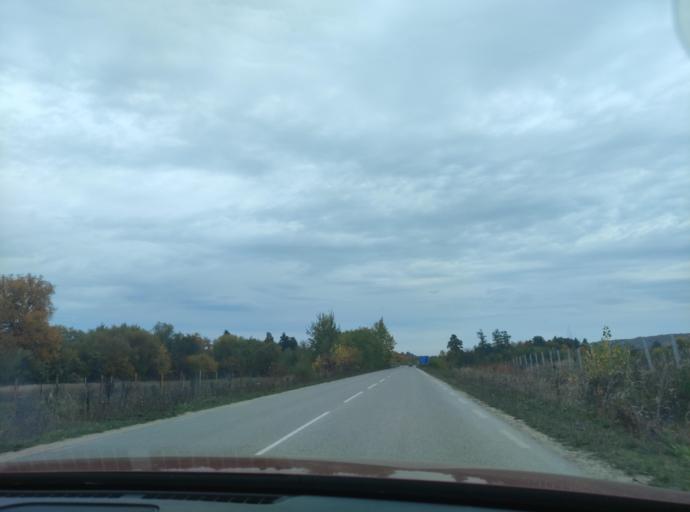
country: BG
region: Montana
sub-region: Obshtina Berkovitsa
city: Berkovitsa
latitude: 43.2406
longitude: 23.1631
